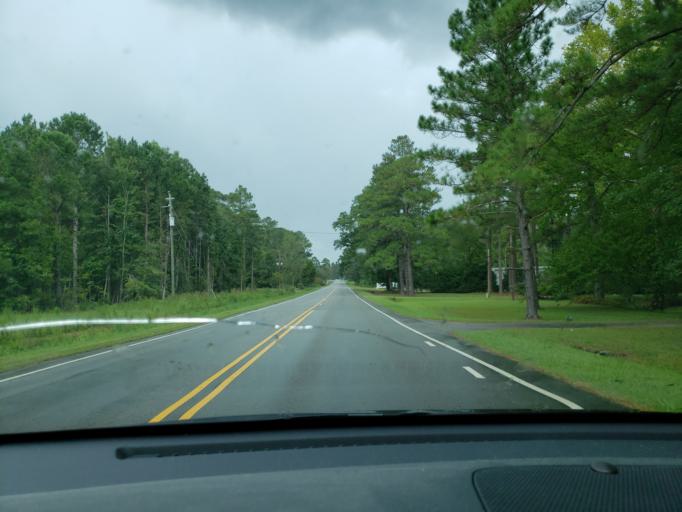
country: US
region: North Carolina
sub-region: Bladen County
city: Elizabethtown
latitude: 34.5073
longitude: -78.6542
